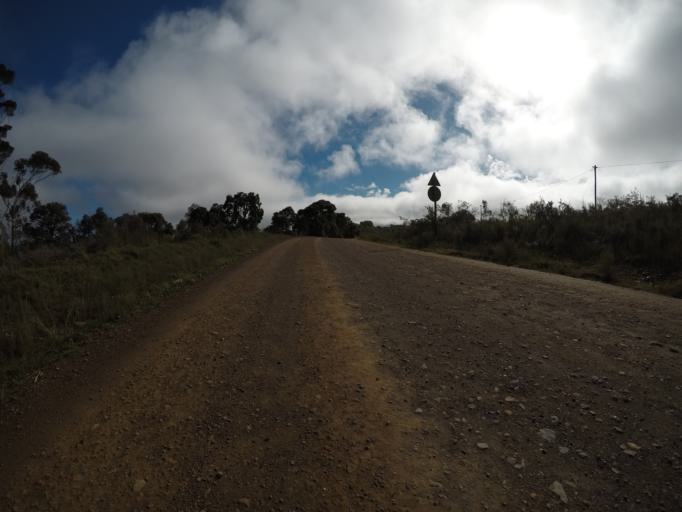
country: ZA
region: Western Cape
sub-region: Cape Winelands District Municipality
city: Ashton
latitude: -34.1219
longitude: 19.8078
